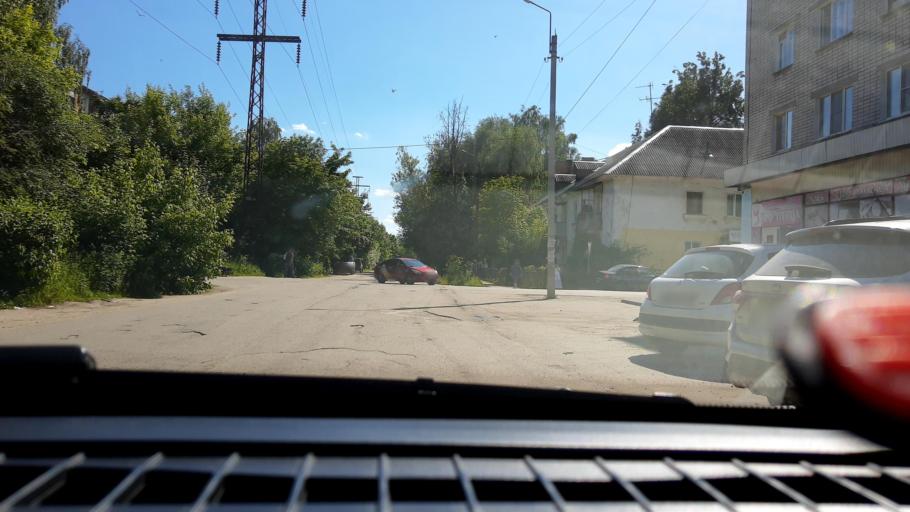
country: RU
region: Nizjnij Novgorod
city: Gidrotorf
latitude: 56.5202
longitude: 43.5550
